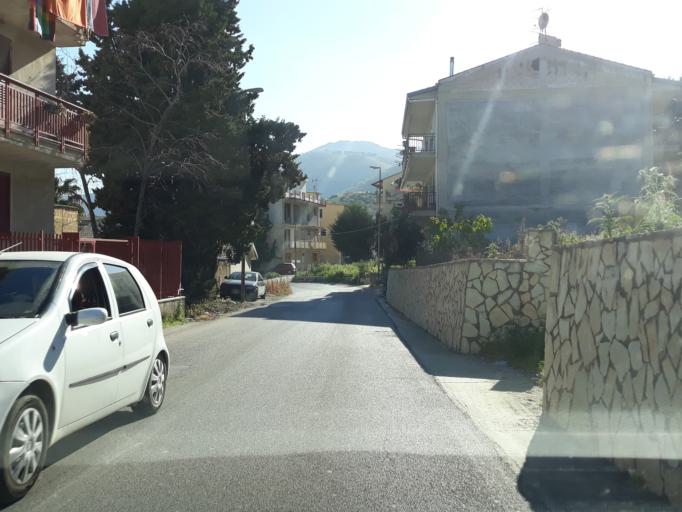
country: IT
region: Sicily
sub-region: Palermo
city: Misilmeri
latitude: 38.0304
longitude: 13.4409
